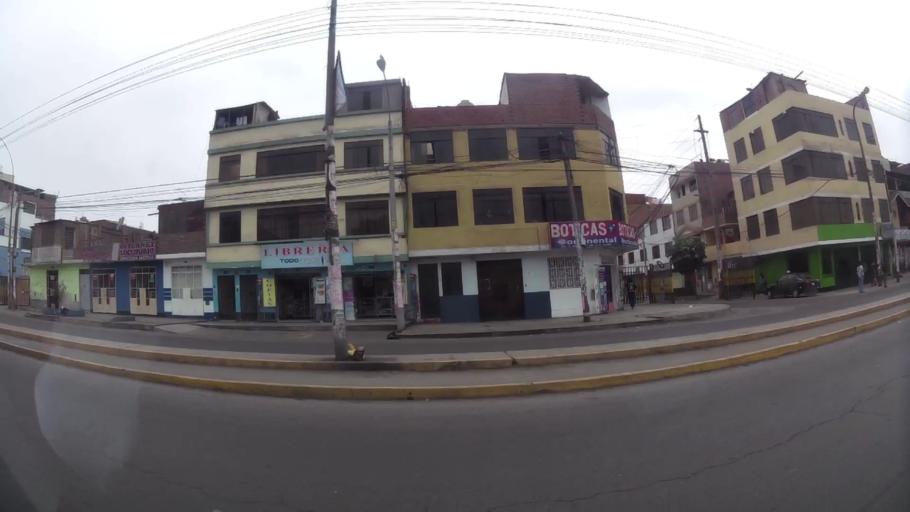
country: PE
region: Lima
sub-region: Lima
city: Independencia
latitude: -11.9990
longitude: -77.0846
